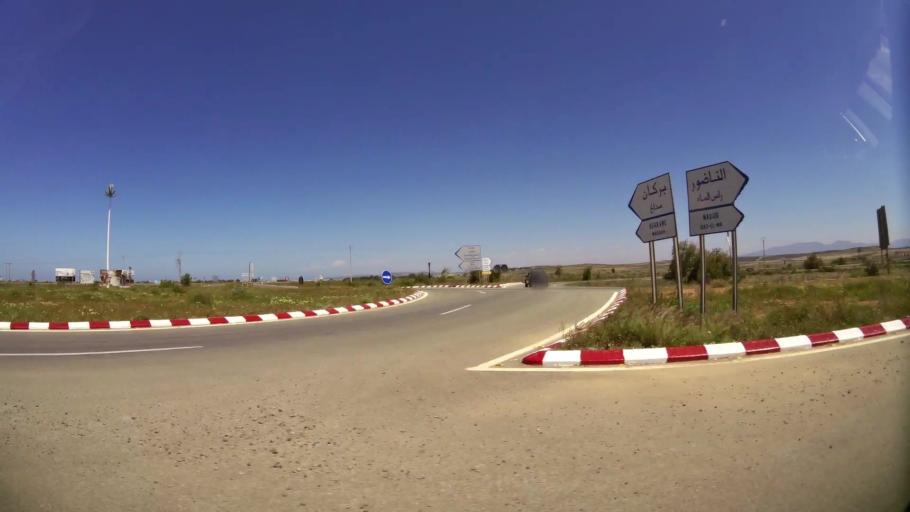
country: MA
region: Oriental
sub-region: Berkane-Taourirt
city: Madagh
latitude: 35.1049
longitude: -2.3513
